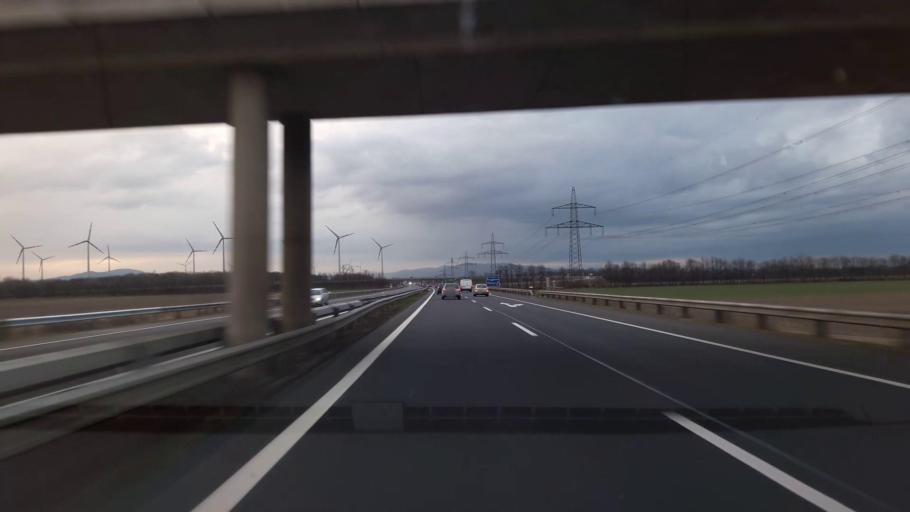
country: AT
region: Lower Austria
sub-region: Politischer Bezirk Baden
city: Ebreichsdorf
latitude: 47.9246
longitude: 16.3971
